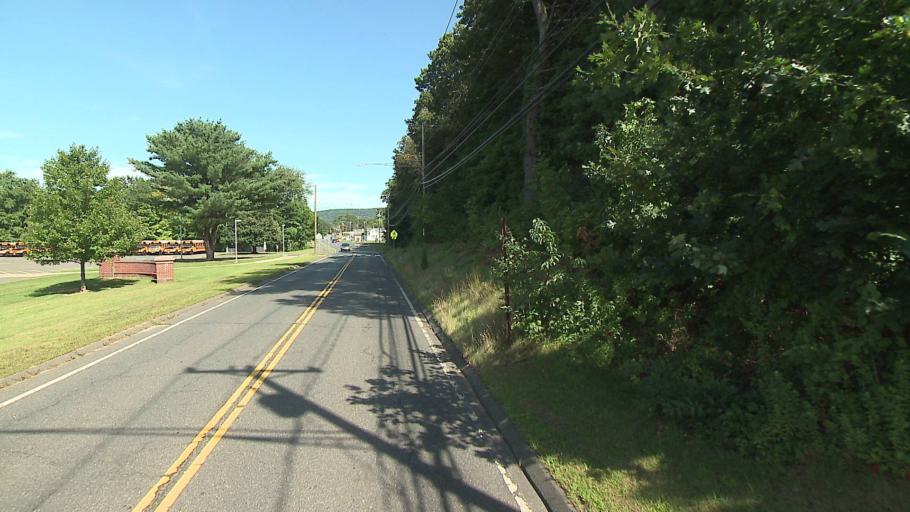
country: US
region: Connecticut
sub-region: Hartford County
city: Simsbury Center
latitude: 41.8699
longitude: -72.8204
